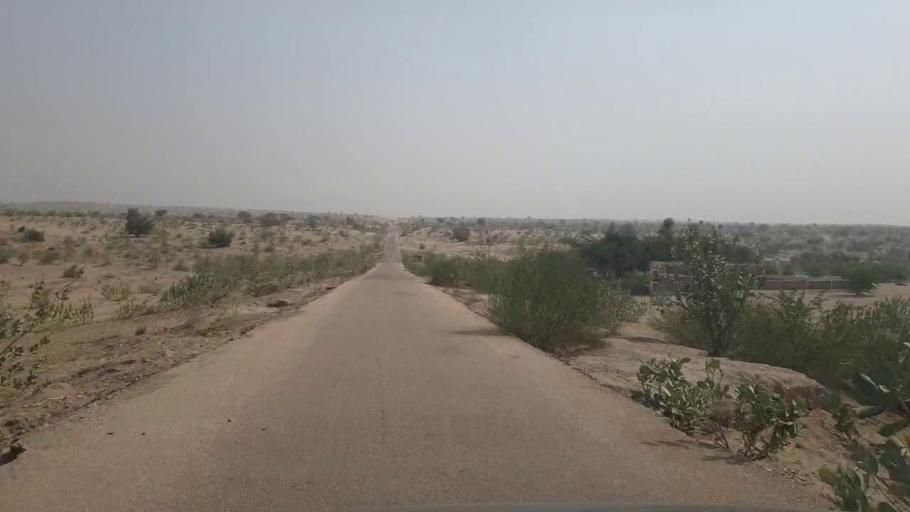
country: PK
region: Sindh
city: Chor
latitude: 25.6004
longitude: 70.0000
